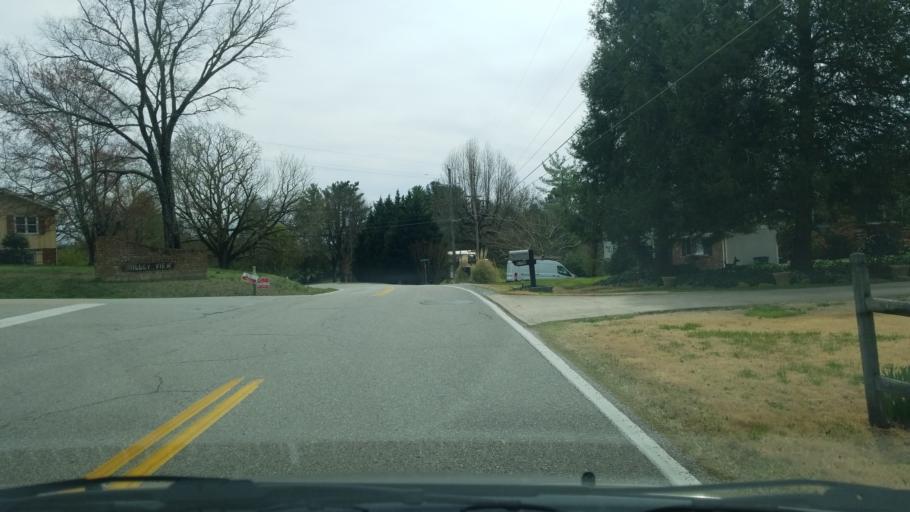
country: US
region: Tennessee
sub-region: Hamilton County
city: East Brainerd
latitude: 35.0167
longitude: -85.1192
